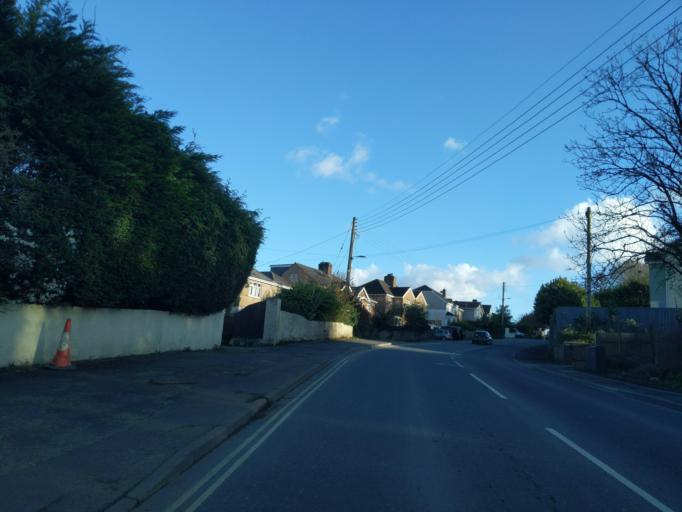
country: GB
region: England
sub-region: Plymouth
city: Plymstock
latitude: 50.3637
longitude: -4.0654
